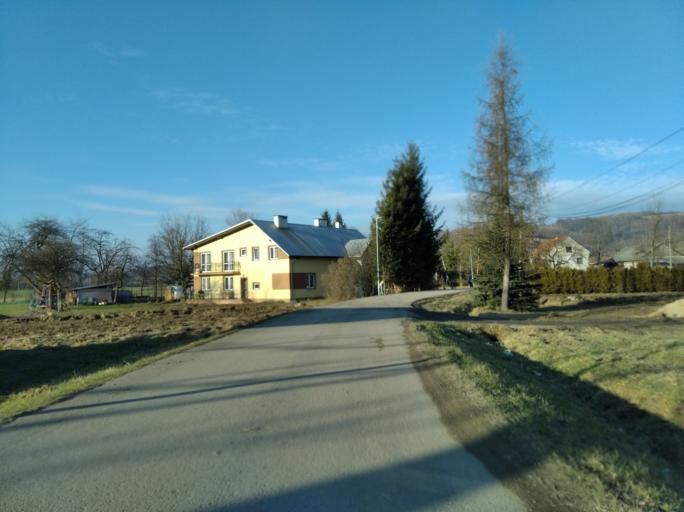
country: PL
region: Subcarpathian Voivodeship
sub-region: Powiat strzyzowski
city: Strzyzow
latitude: 49.8338
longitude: 21.8354
